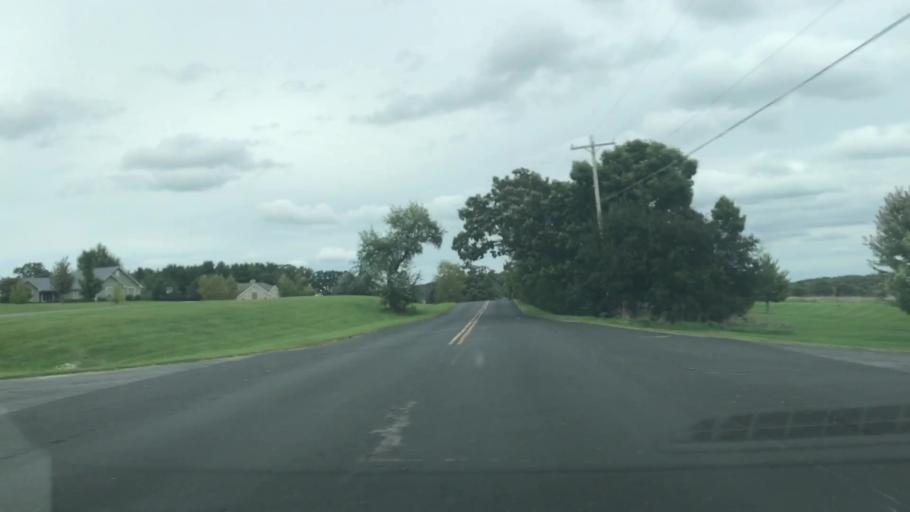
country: US
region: Wisconsin
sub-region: Waukesha County
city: North Prairie
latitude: 42.9151
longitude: -88.4133
